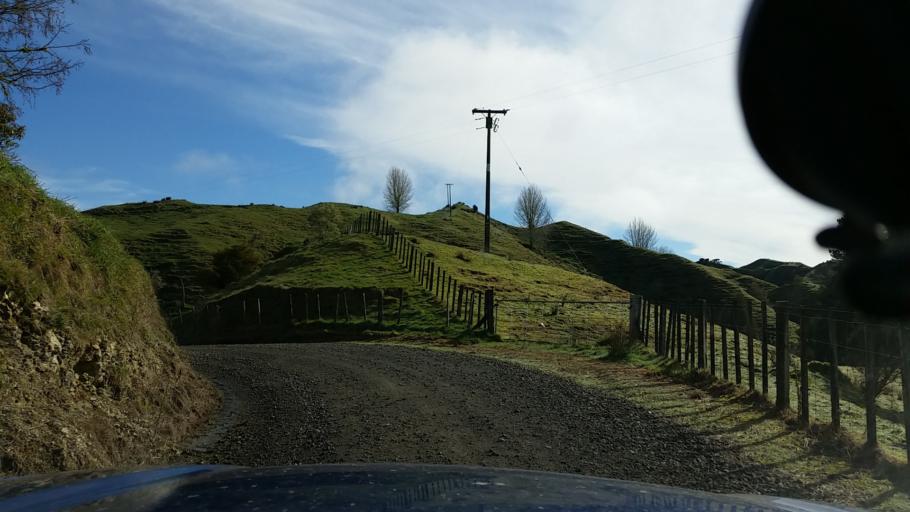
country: NZ
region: Taranaki
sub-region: New Plymouth District
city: Waitara
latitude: -39.0330
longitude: 174.7777
